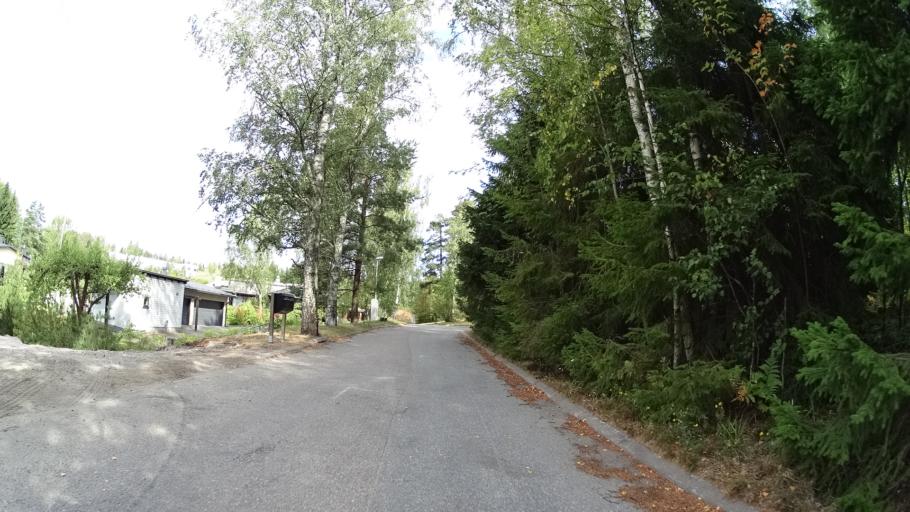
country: FI
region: Uusimaa
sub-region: Helsinki
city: Koukkuniemi
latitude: 60.1655
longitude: 24.7626
